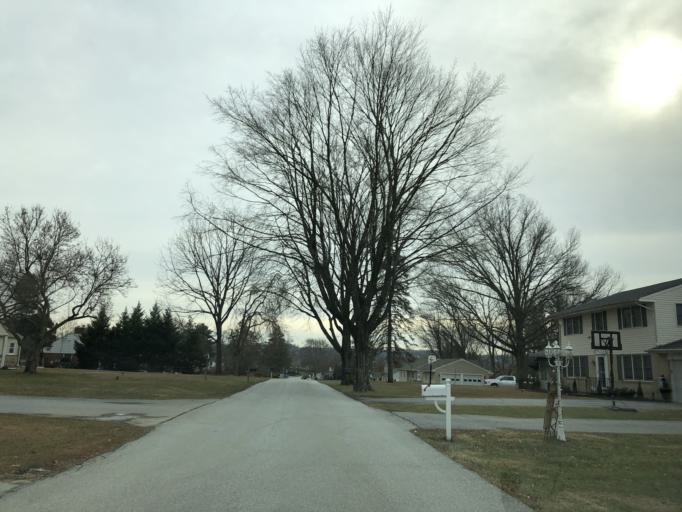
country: US
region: Pennsylvania
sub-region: Chester County
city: Exton
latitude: 40.0367
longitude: -75.6269
